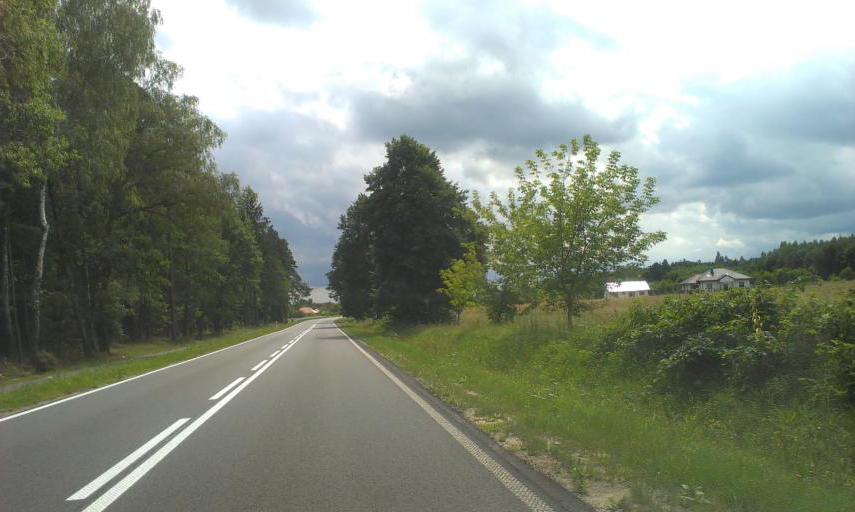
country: PL
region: West Pomeranian Voivodeship
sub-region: Koszalin
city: Koszalin
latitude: 54.0755
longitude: 16.1623
